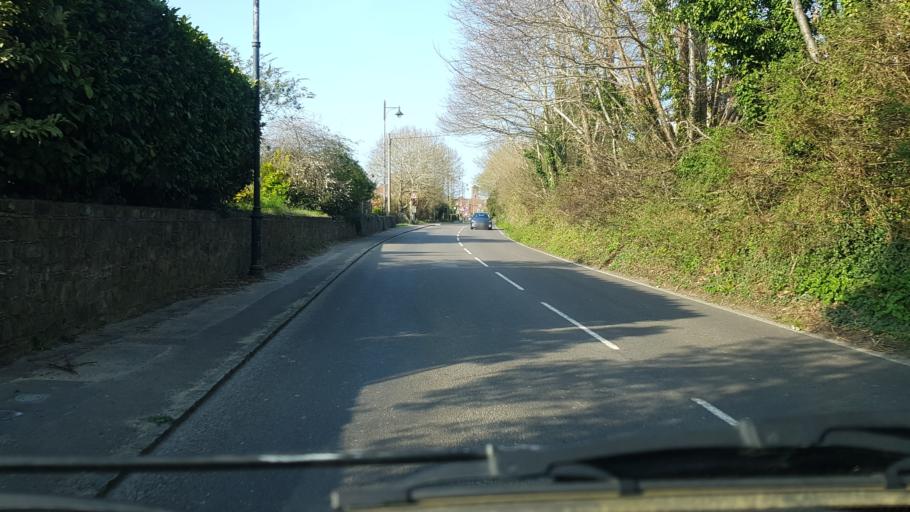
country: GB
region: England
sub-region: West Sussex
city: Petworth
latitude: 50.9806
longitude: -0.6122
